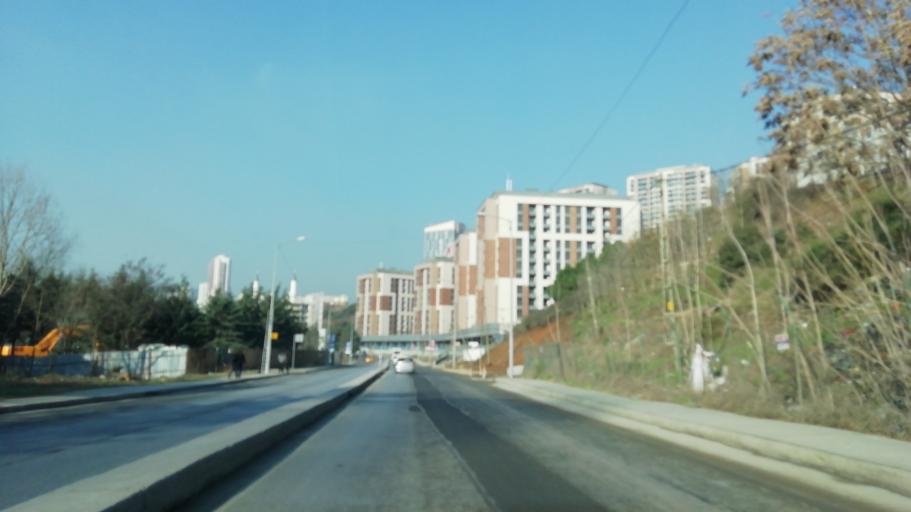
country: TR
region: Istanbul
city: Sisli
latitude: 41.0862
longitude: 28.9511
